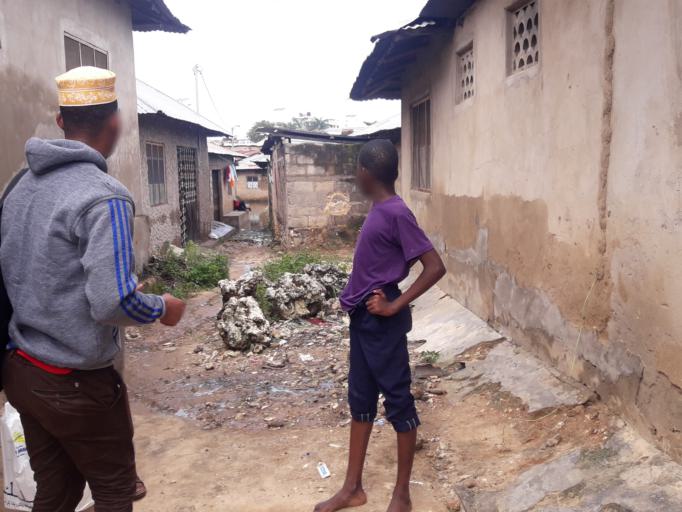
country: TZ
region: Zanzibar Urban/West
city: Zanzibar
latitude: -6.1718
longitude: 39.2234
